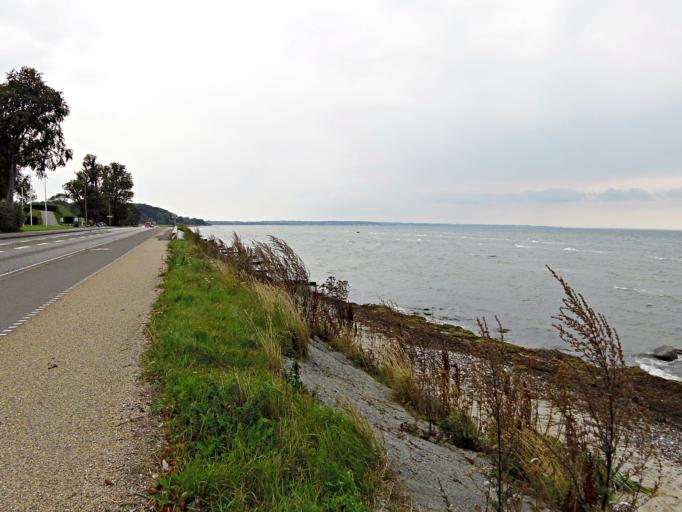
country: DK
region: Capital Region
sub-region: Fredensborg Kommune
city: Kokkedal
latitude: 55.8987
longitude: 12.5344
